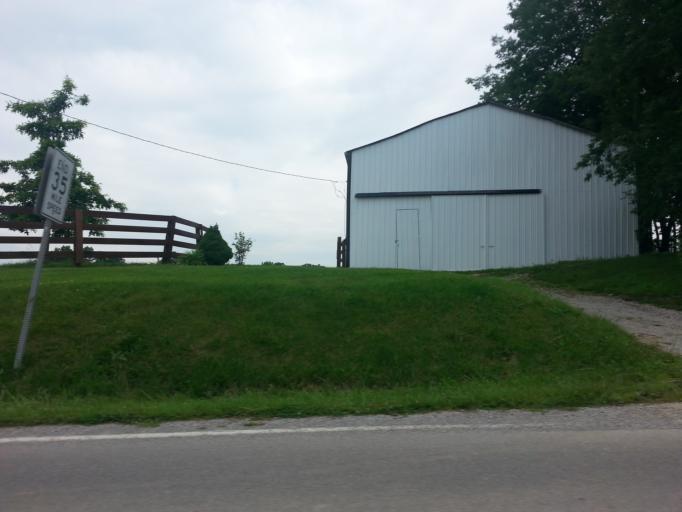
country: US
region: Kentucky
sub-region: Robertson County
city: Mount Olivet
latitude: 38.5327
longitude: -84.0237
